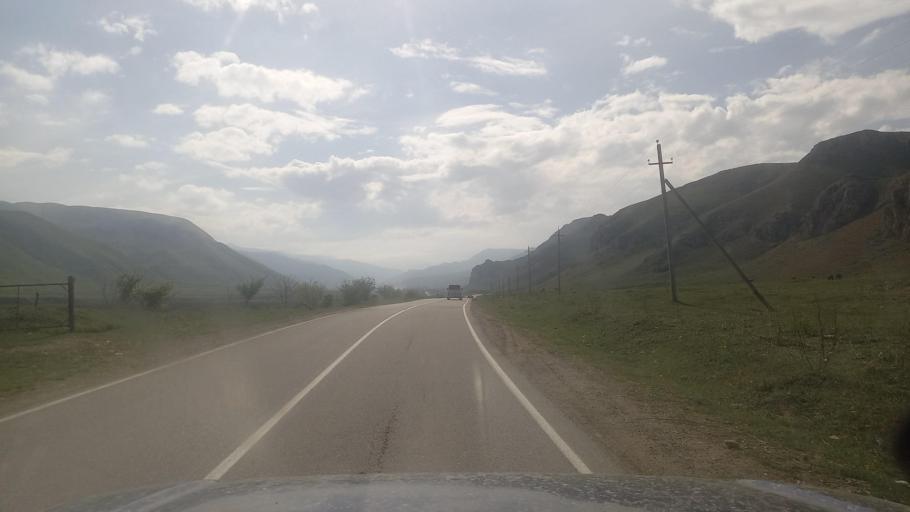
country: RU
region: Kabardino-Balkariya
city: Kamennomostskoye
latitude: 43.7346
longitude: 42.9799
